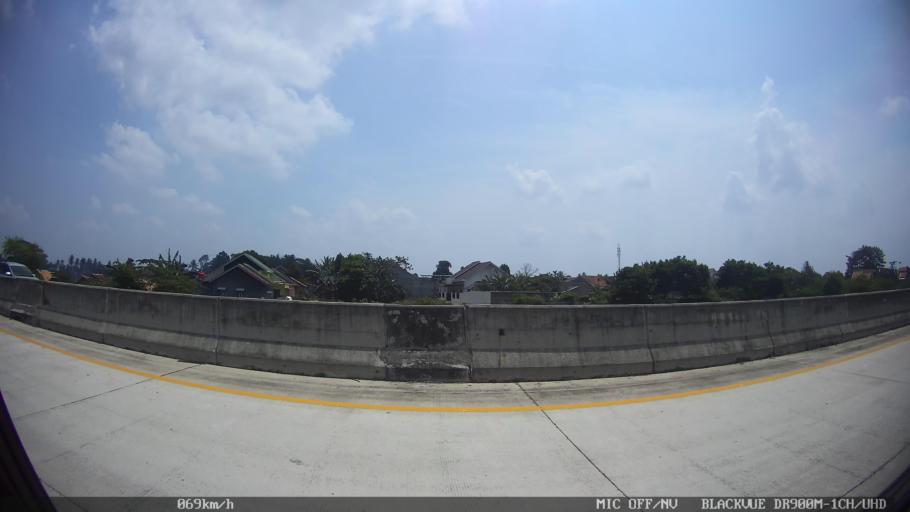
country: ID
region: Lampung
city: Kedaton
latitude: -5.3291
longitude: 105.2869
